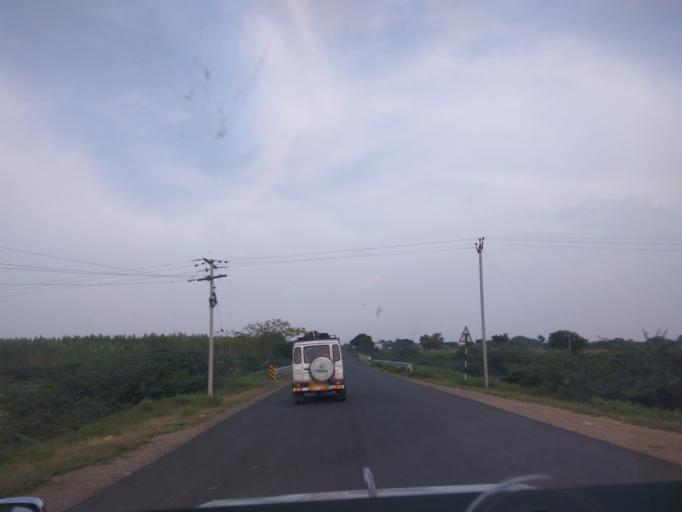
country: IN
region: Andhra Pradesh
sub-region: Guntur
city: Vinukonda
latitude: 16.0164
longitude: 79.5526
